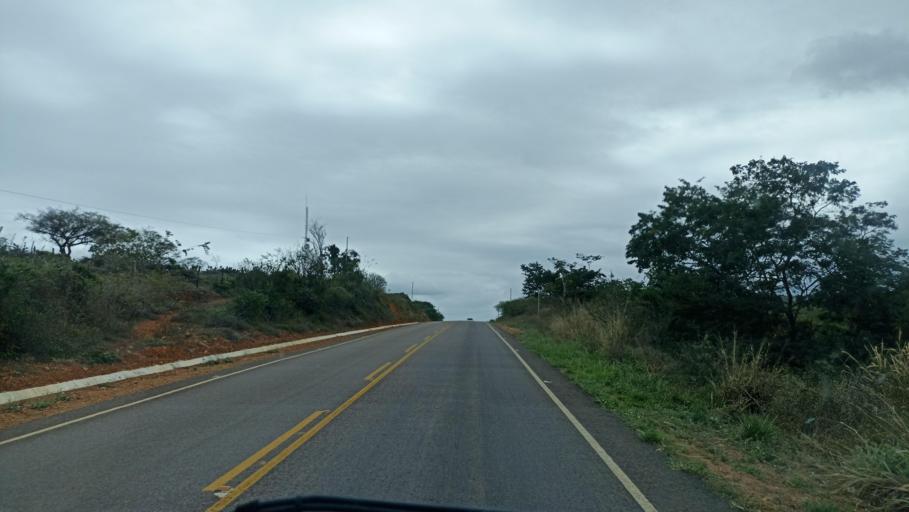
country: BR
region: Bahia
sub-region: Andarai
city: Vera Cruz
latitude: -12.9923
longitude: -41.0005
